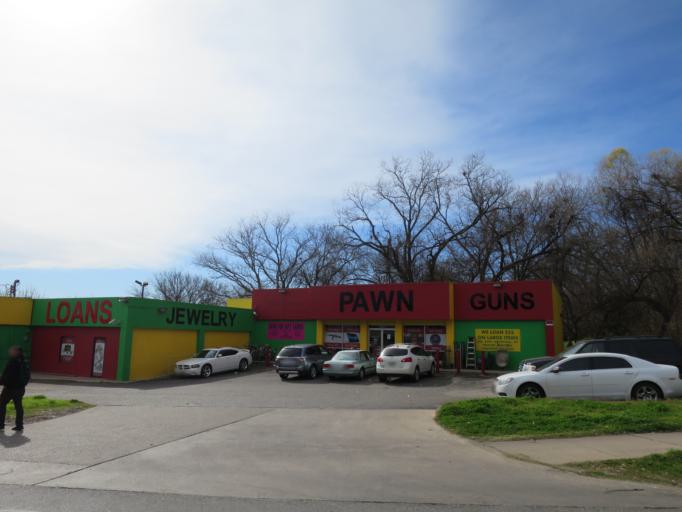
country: US
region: Texas
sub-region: Travis County
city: Austin
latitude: 30.2743
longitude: -97.6983
